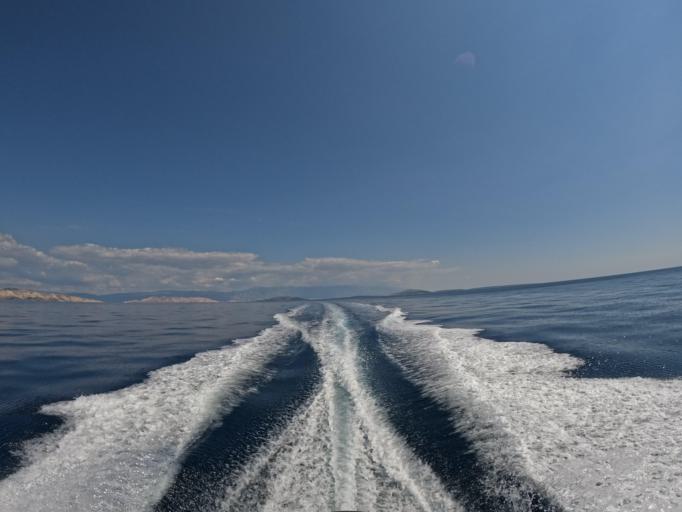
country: HR
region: Primorsko-Goranska
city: Punat
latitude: 44.9126
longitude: 14.5861
